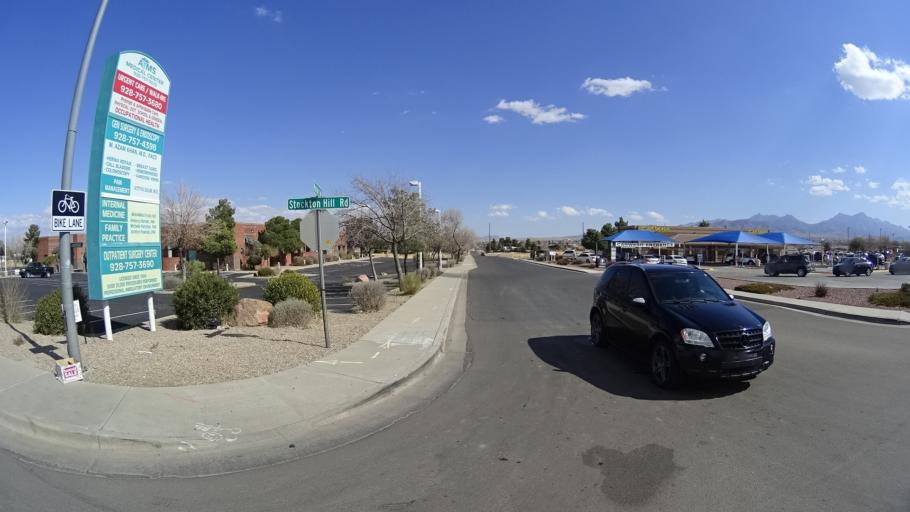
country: US
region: Arizona
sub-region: Mohave County
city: New Kingman-Butler
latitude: 35.2287
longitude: -114.0366
